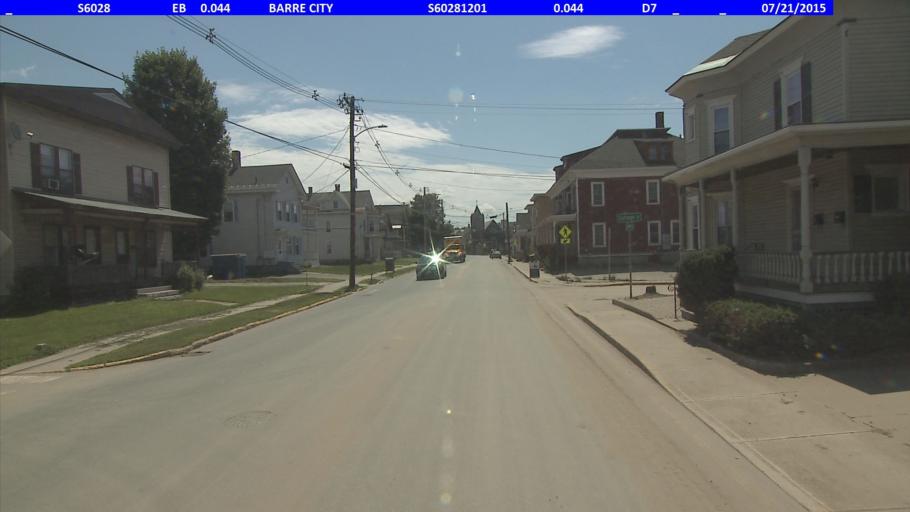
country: US
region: Vermont
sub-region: Washington County
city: Barre
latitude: 44.2028
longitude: -72.5061
